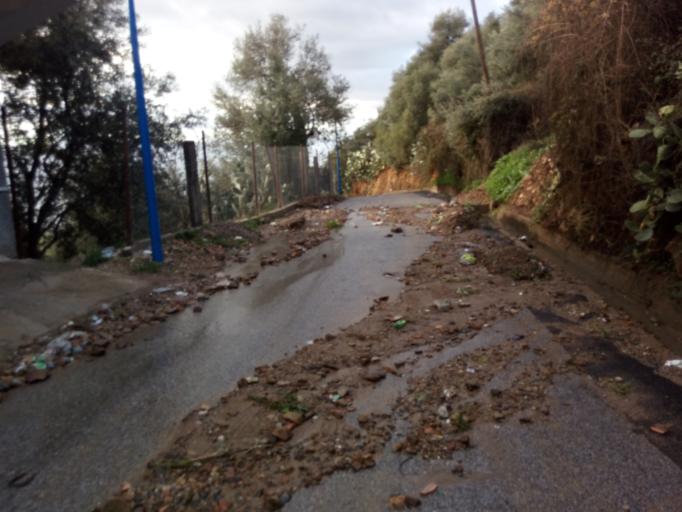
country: DZ
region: Tizi Ouzou
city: Chemini
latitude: 36.6041
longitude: 4.6385
